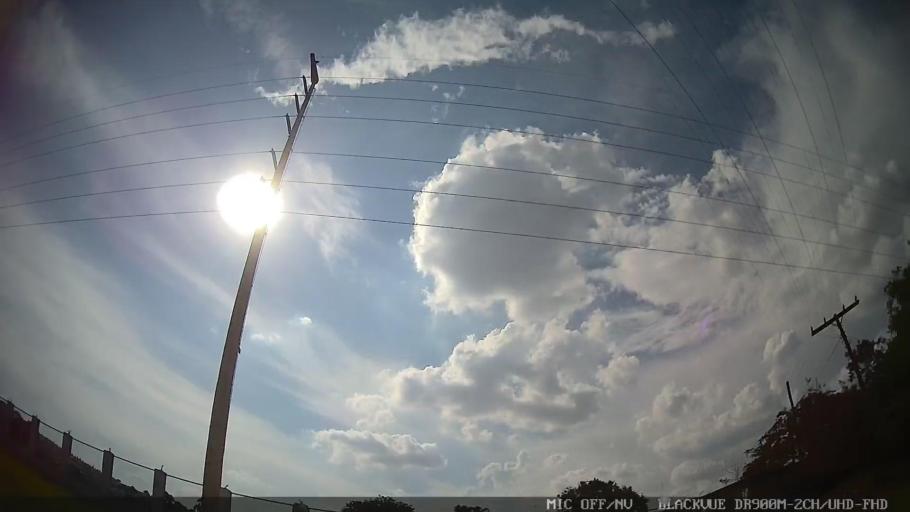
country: BR
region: Sao Paulo
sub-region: Braganca Paulista
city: Braganca Paulista
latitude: -22.9297
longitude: -46.5552
